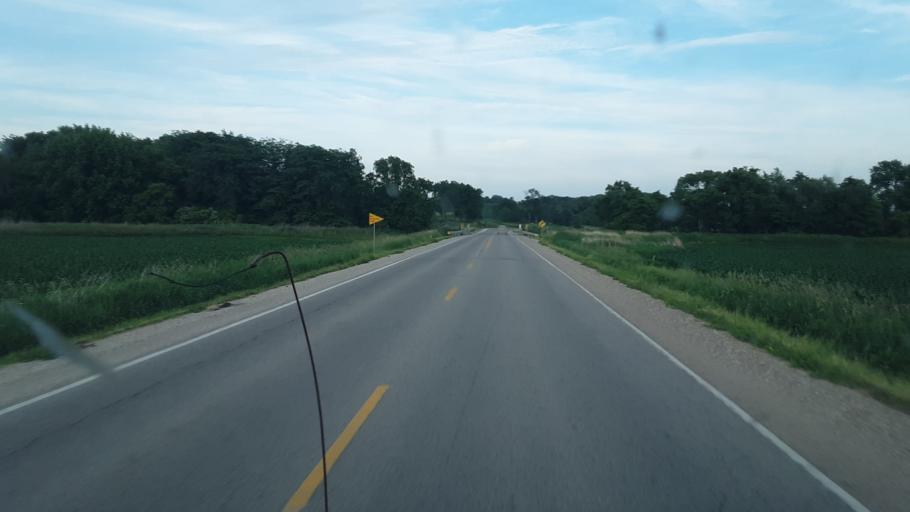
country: US
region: Iowa
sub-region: Benton County
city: Belle Plaine
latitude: 41.9196
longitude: -92.3628
